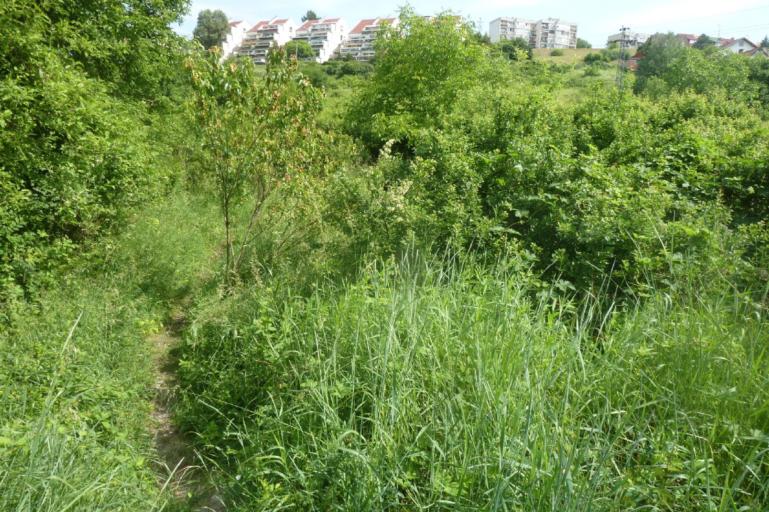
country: HU
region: Pest
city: Szentendre
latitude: 47.6653
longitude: 19.0568
